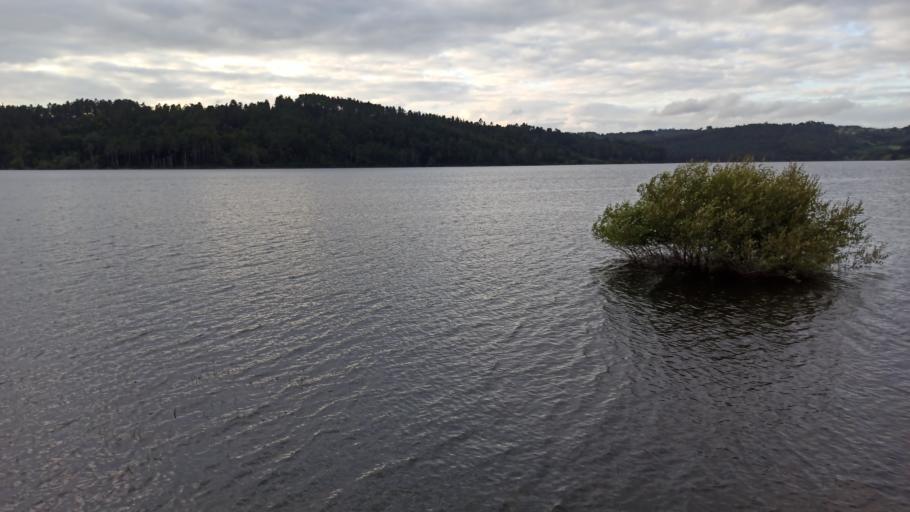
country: ES
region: Galicia
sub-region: Provincia da Coruna
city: Santiso
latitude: 42.8361
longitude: -8.1234
